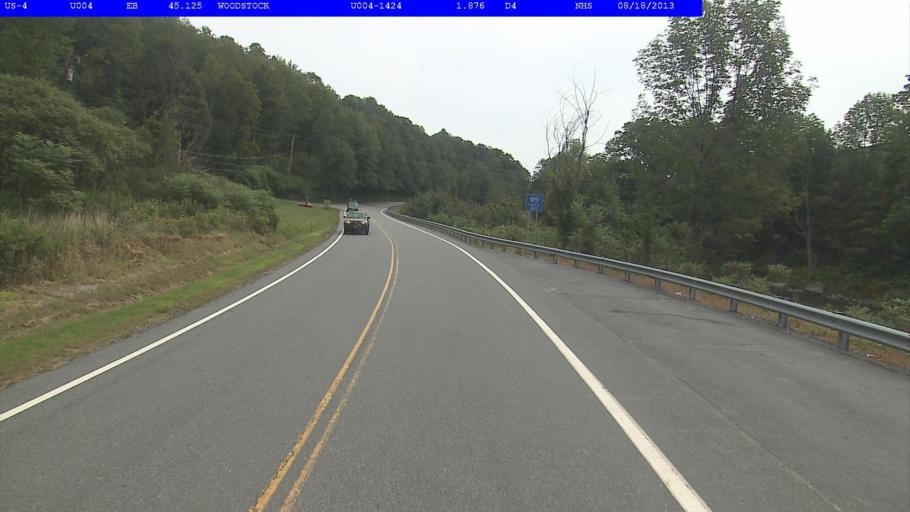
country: US
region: Vermont
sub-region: Windsor County
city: Woodstock
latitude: 43.5999
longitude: -72.5915
